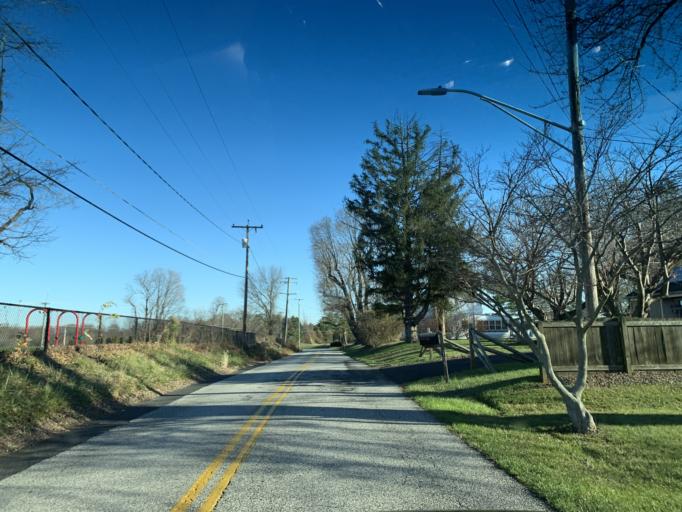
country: US
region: Maryland
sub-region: Harford County
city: Riverside
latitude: 39.5608
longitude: -76.2444
